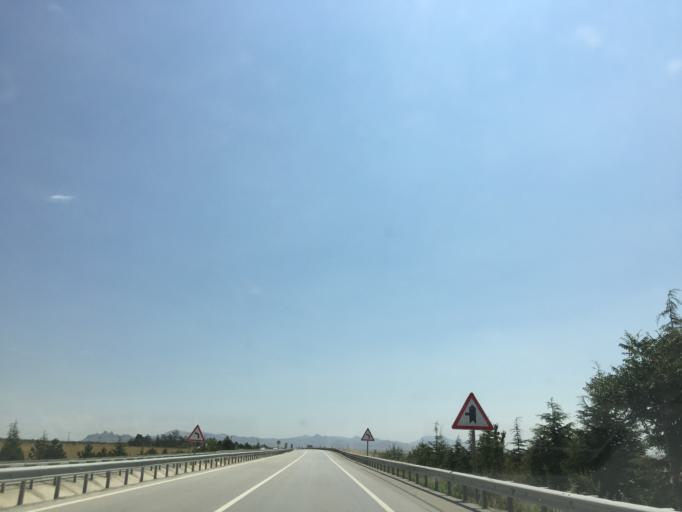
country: TR
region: Eskisehir
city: Sivrihisar
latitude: 39.4585
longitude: 31.3885
